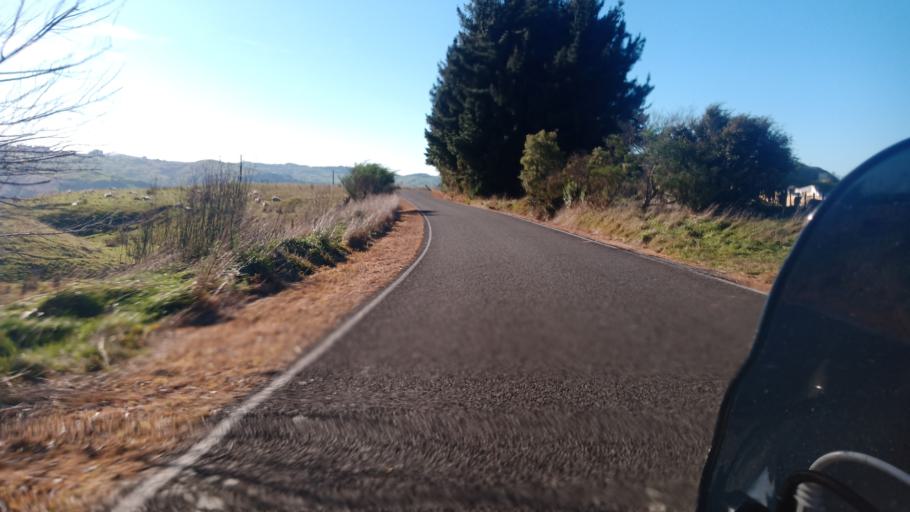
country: NZ
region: Hawke's Bay
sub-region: Wairoa District
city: Wairoa
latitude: -38.8324
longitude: 177.2773
